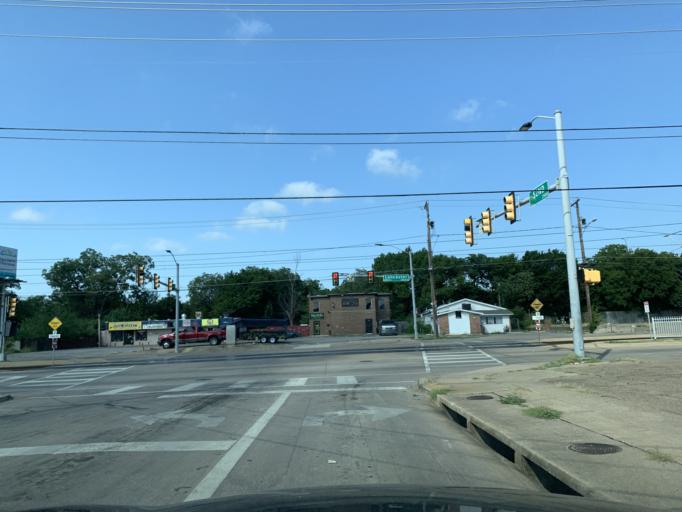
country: US
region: Texas
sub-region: Dallas County
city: Hutchins
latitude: 32.6898
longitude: -96.7910
